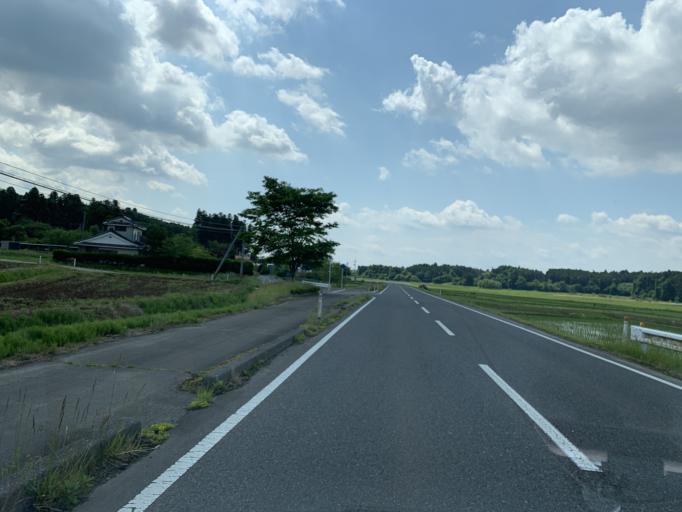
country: JP
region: Miyagi
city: Furukawa
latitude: 38.6752
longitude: 140.9842
